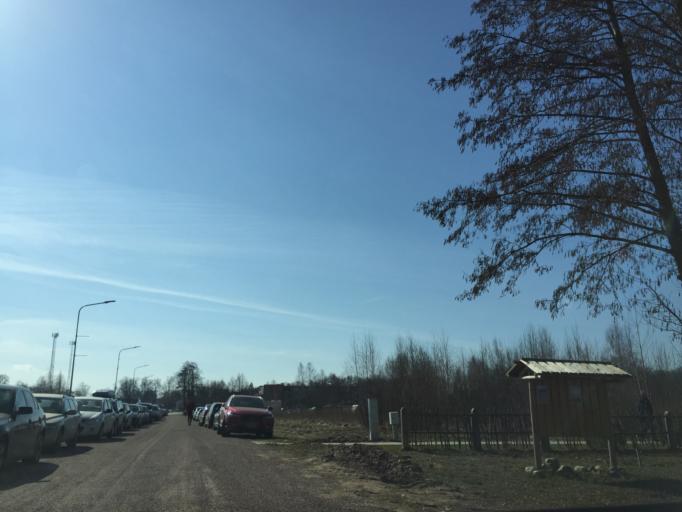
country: LV
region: Carnikava
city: Carnikava
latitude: 57.1321
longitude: 24.2825
